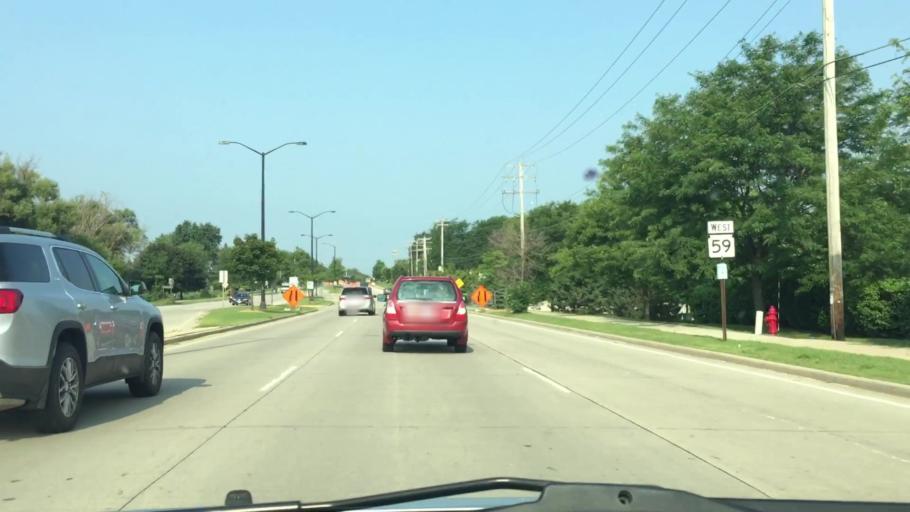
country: US
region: Wisconsin
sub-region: Waukesha County
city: Elm Grove
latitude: 43.0169
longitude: -88.1081
